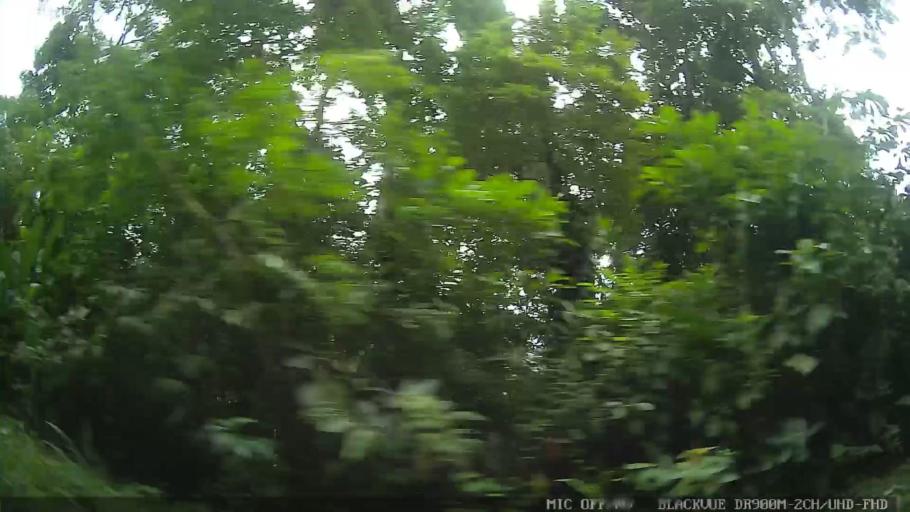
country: BR
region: Sao Paulo
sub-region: Iguape
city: Iguape
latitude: -24.6861
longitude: -47.5070
